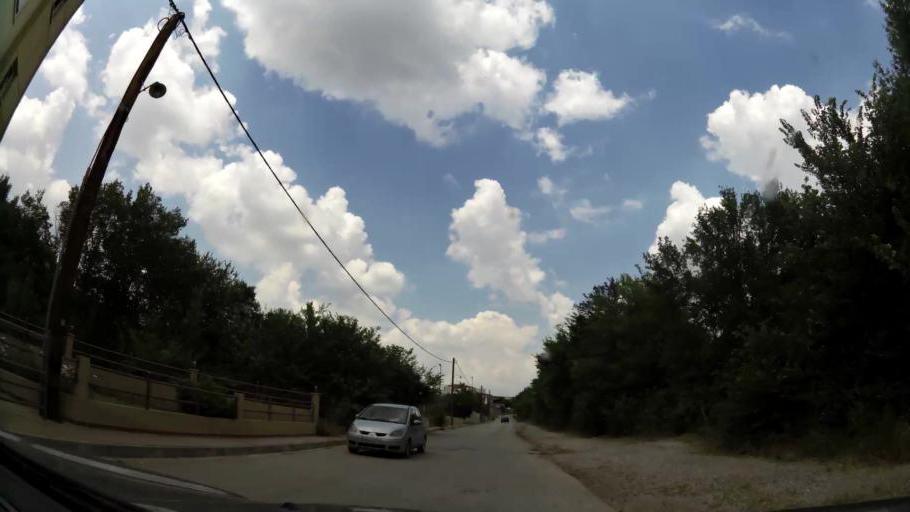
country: GR
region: West Macedonia
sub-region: Nomos Kozanis
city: Kozani
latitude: 40.3006
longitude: 21.8050
